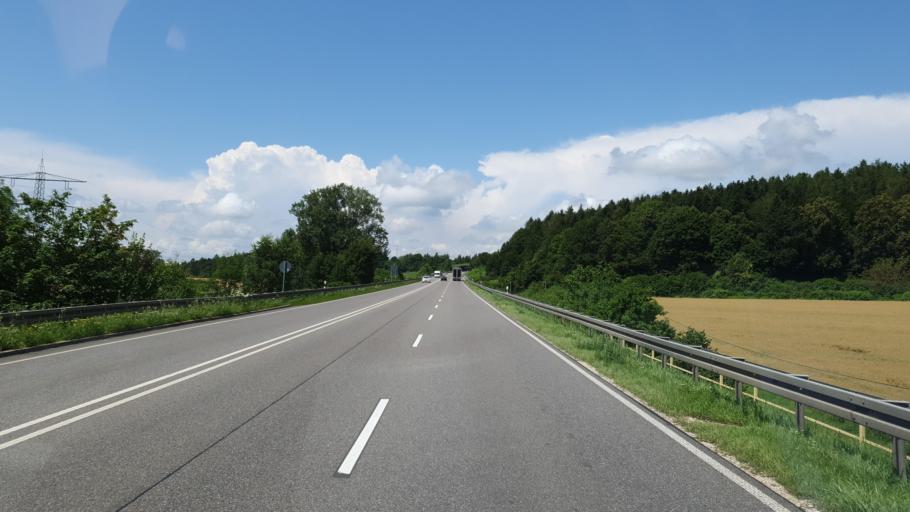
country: DE
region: Baden-Wuerttemberg
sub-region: Freiburg Region
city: Bodman-Ludwigshafen
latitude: 47.8245
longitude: 9.0785
